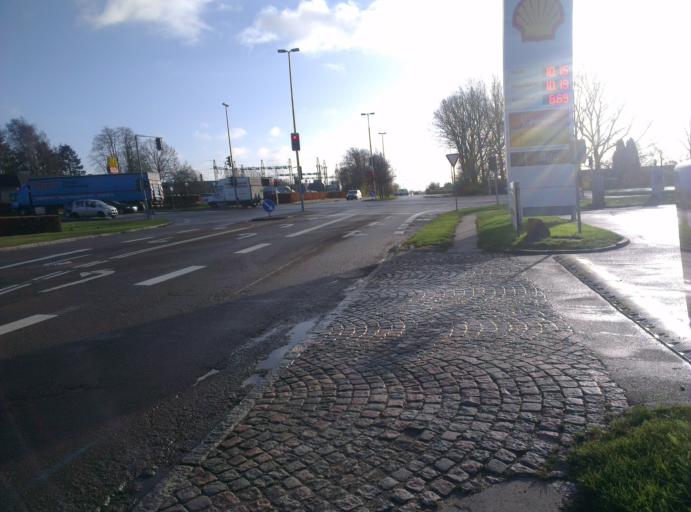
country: DK
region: Capital Region
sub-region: Frederikssund Kommune
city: Frederikssund
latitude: 55.8441
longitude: 12.0742
